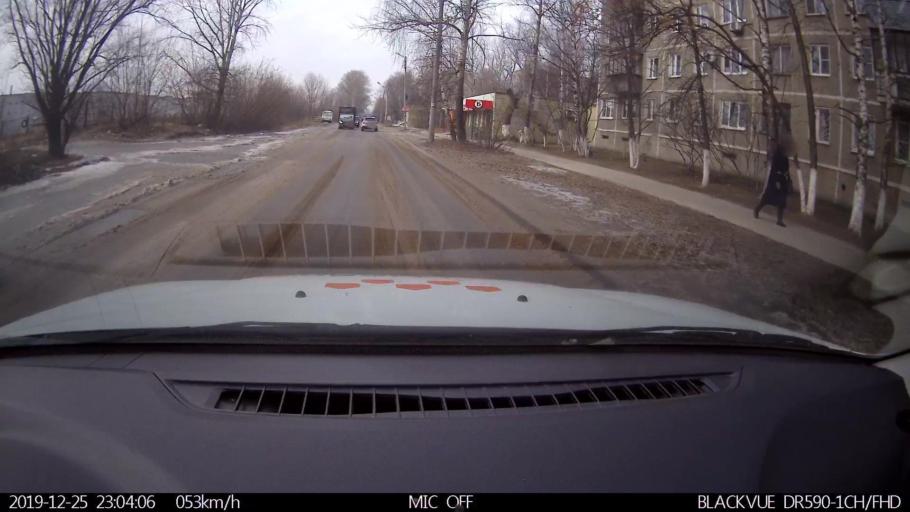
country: RU
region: Nizjnij Novgorod
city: Gorbatovka
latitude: 56.3567
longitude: 43.8143
